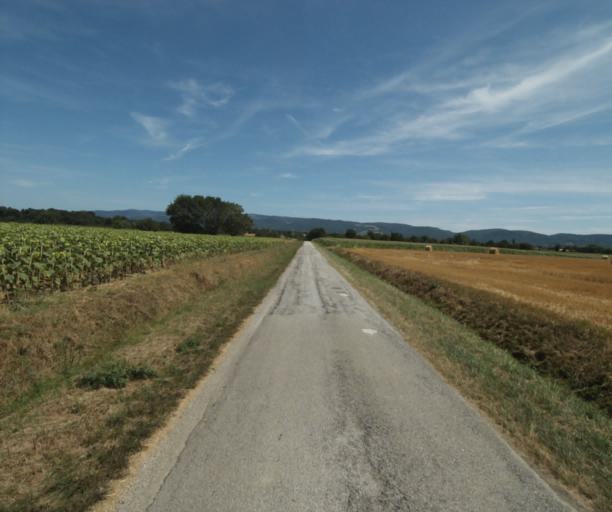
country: FR
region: Midi-Pyrenees
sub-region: Departement de la Haute-Garonne
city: Revel
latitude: 43.4965
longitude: 2.0128
